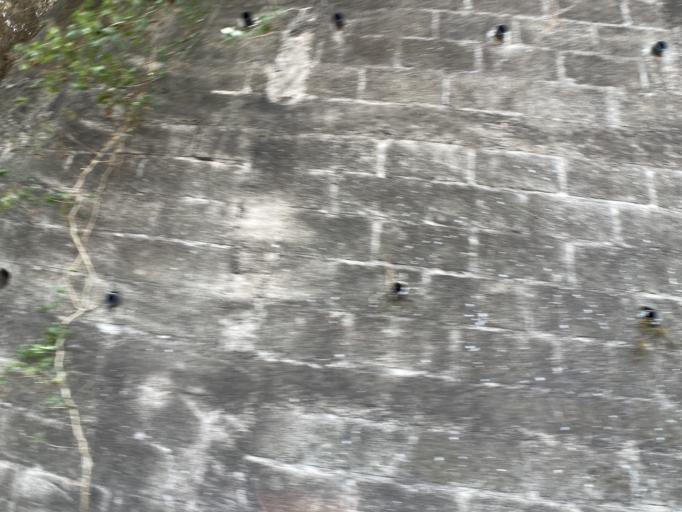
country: GT
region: Santa Rosa
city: Pueblo Nuevo Vinas
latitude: 14.3182
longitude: -90.5352
